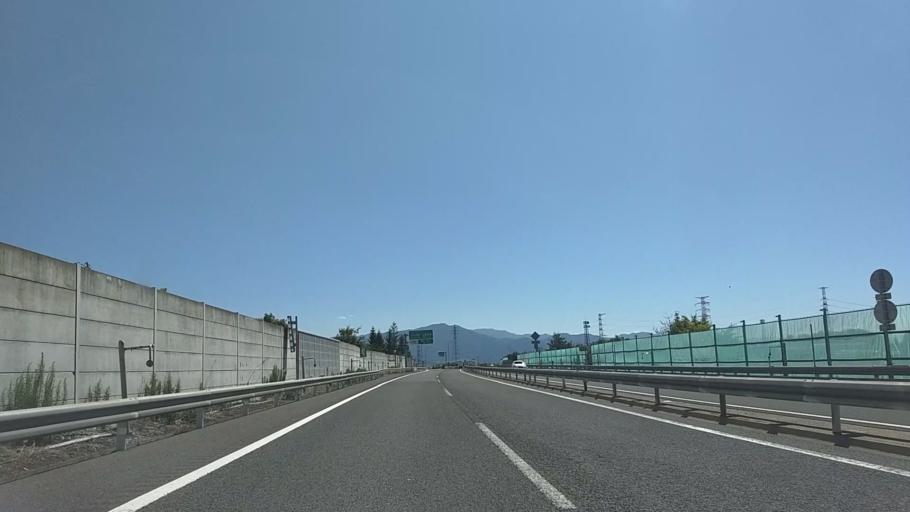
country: JP
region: Nagano
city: Nakano
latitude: 36.7344
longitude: 138.3181
